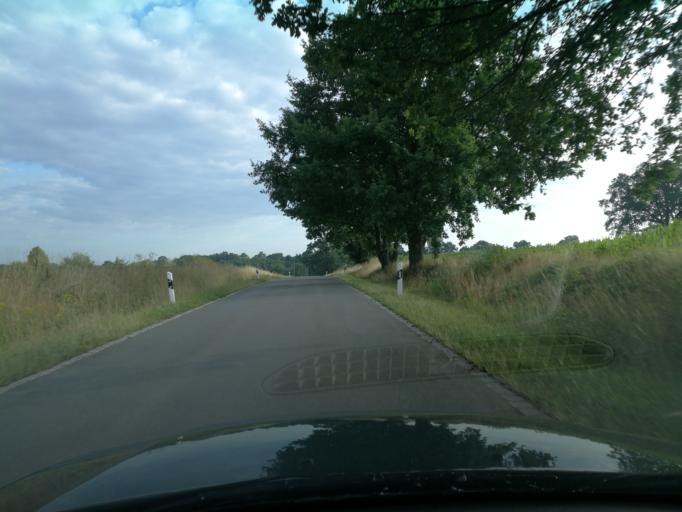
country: DE
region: Bavaria
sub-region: Regierungsbezirk Mittelfranken
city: Obermichelbach
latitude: 49.5214
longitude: 10.9524
